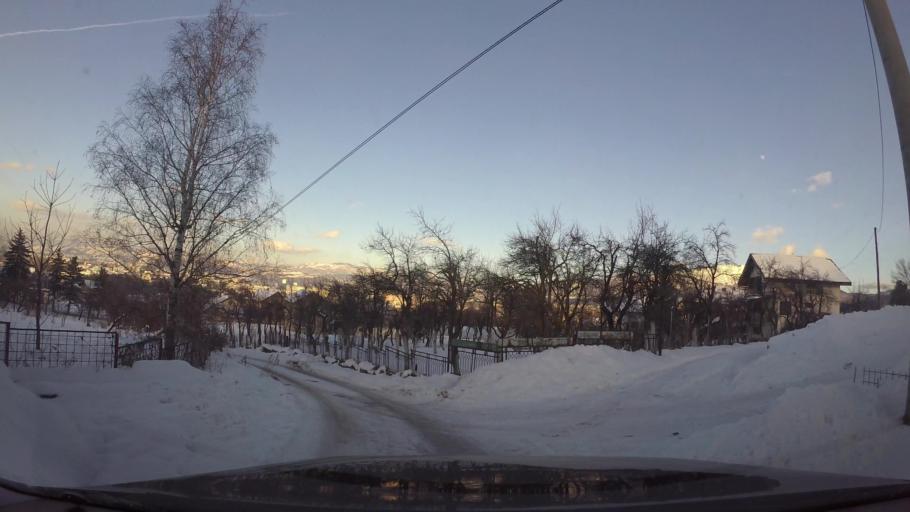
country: BA
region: Federation of Bosnia and Herzegovina
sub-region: Kanton Sarajevo
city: Sarajevo
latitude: 43.8085
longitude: 18.3536
